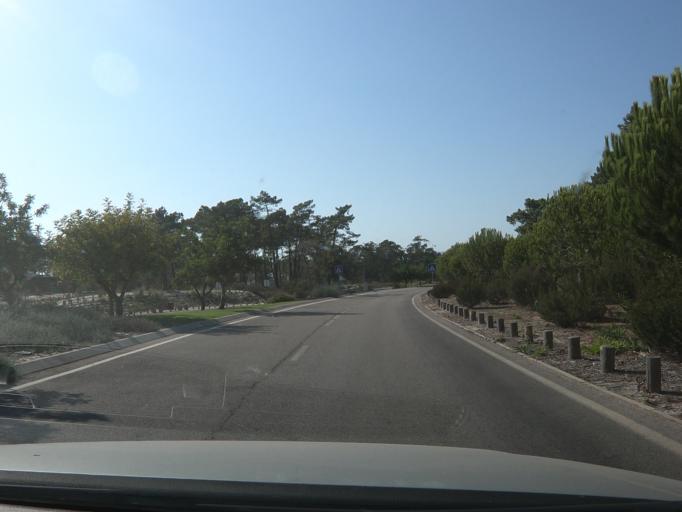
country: PT
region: Setubal
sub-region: Setubal
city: Setubal
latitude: 38.4657
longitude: -8.8729
